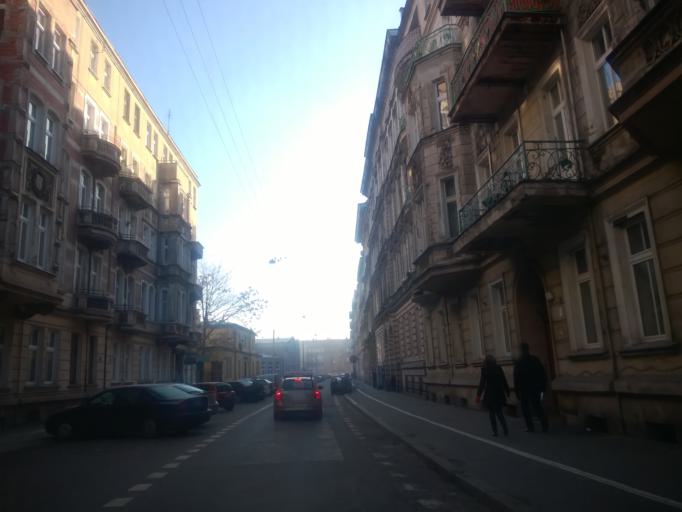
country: PL
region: Lower Silesian Voivodeship
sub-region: Powiat wroclawski
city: Wroclaw
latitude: 51.1043
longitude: 17.0441
